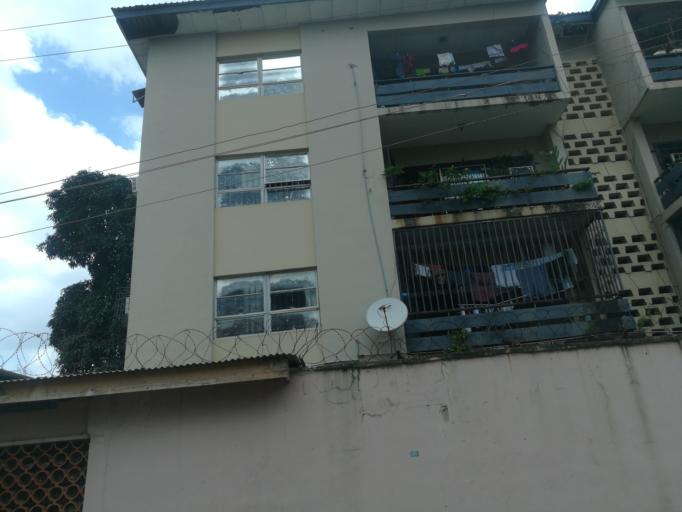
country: NG
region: Lagos
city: Somolu
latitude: 6.5564
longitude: 3.3655
